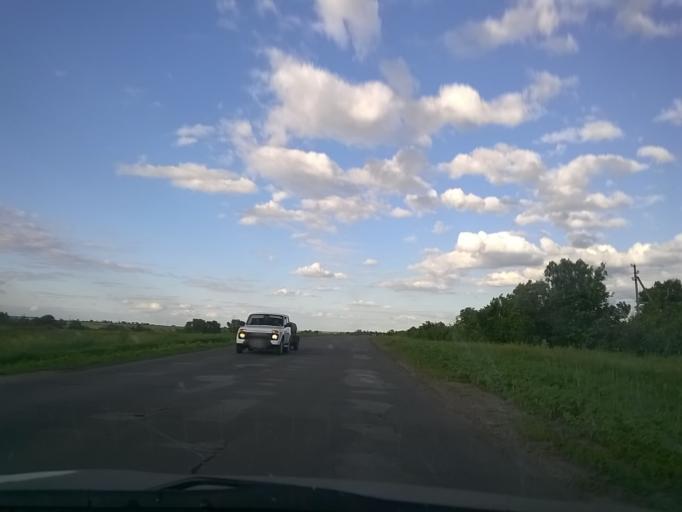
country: RU
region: Volgograd
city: Uryupinsk
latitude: 50.8331
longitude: 42.0833
